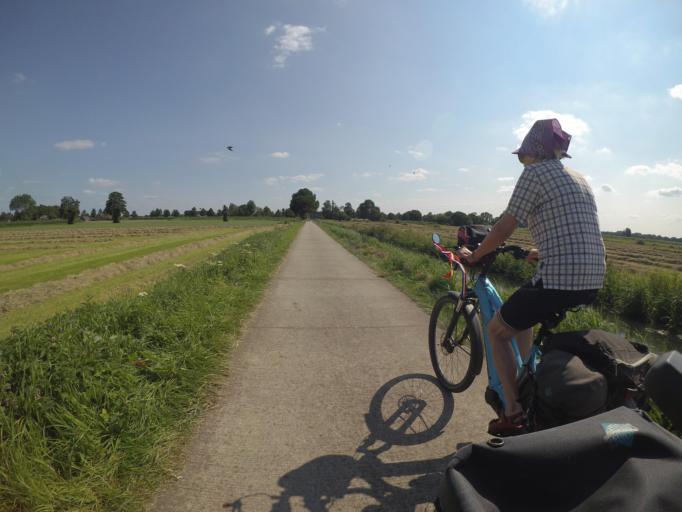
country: NL
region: Gelderland
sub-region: Gemeente Epe
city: Oene
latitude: 52.3563
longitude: 6.0419
